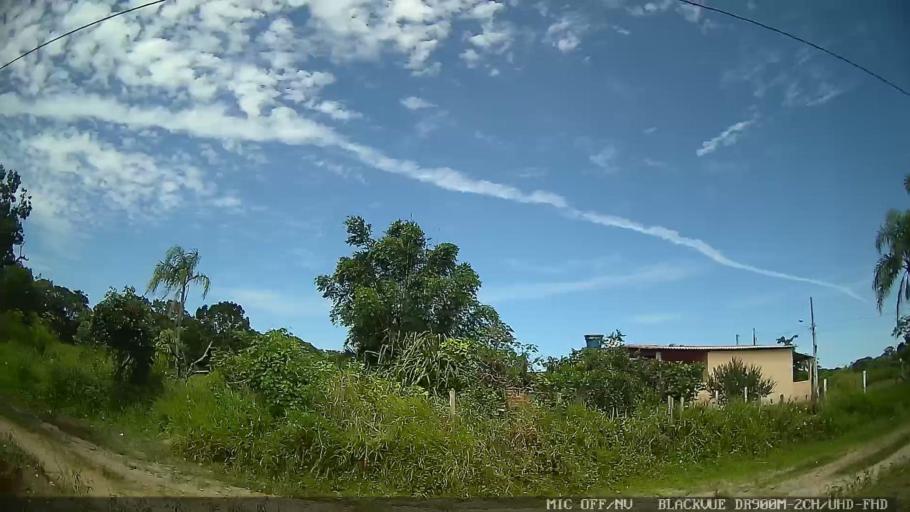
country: BR
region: Sao Paulo
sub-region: Iguape
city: Iguape
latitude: -24.7183
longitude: -47.5241
